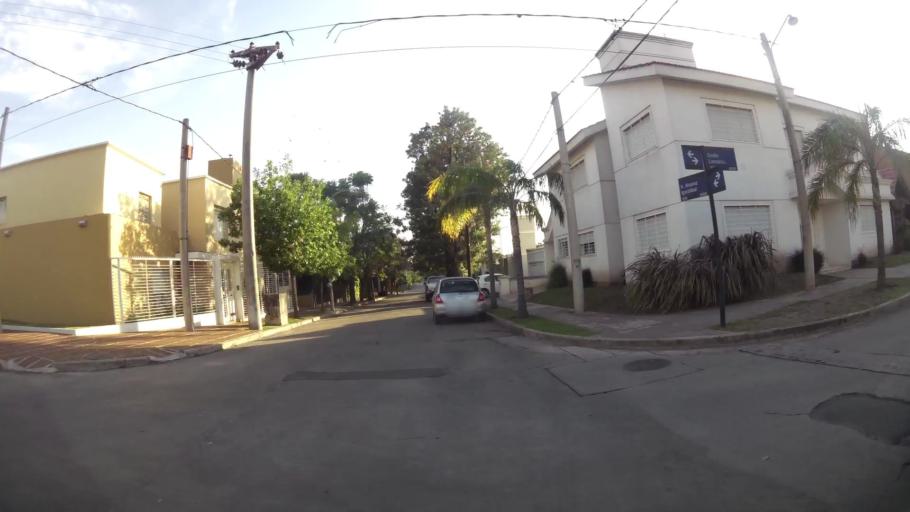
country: AR
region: Cordoba
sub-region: Departamento de Capital
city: Cordoba
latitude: -31.3837
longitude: -64.2406
